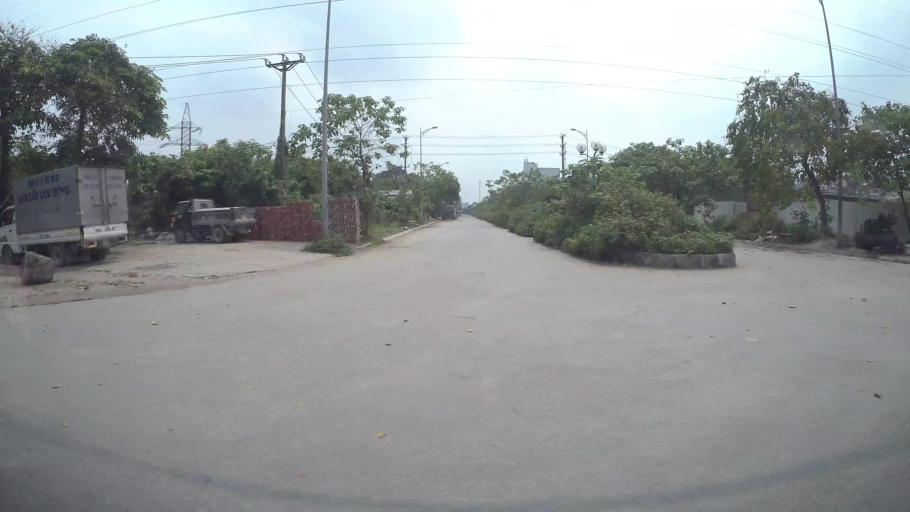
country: VN
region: Ha Noi
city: Trau Quy
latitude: 21.0690
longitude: 105.9030
